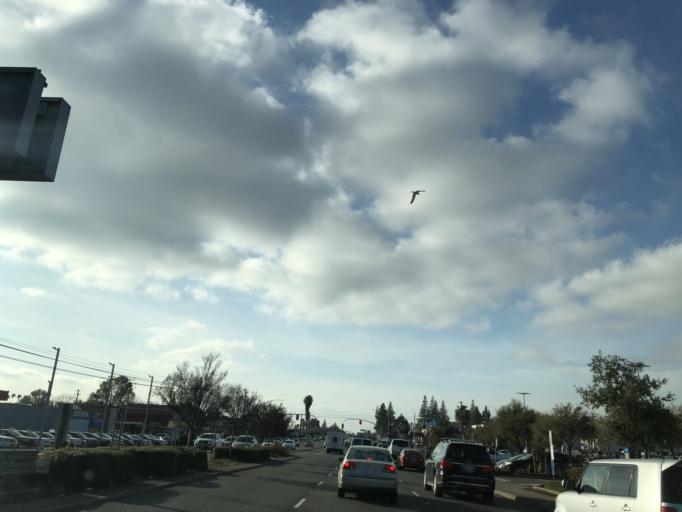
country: US
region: California
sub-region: Sacramento County
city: Foothill Farms
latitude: 38.6610
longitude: -121.3488
